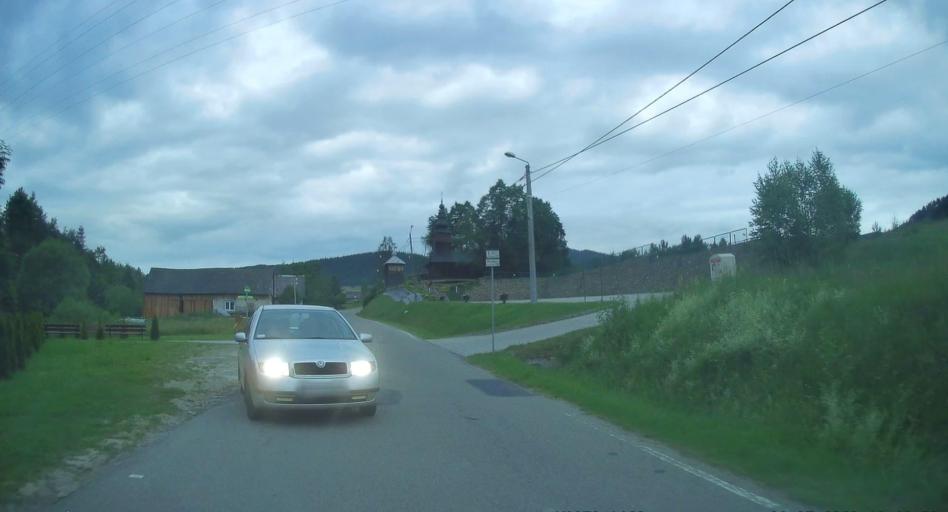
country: PL
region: Lesser Poland Voivodeship
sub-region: Powiat nowosadecki
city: Muszyna
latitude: 49.3847
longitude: 20.9171
